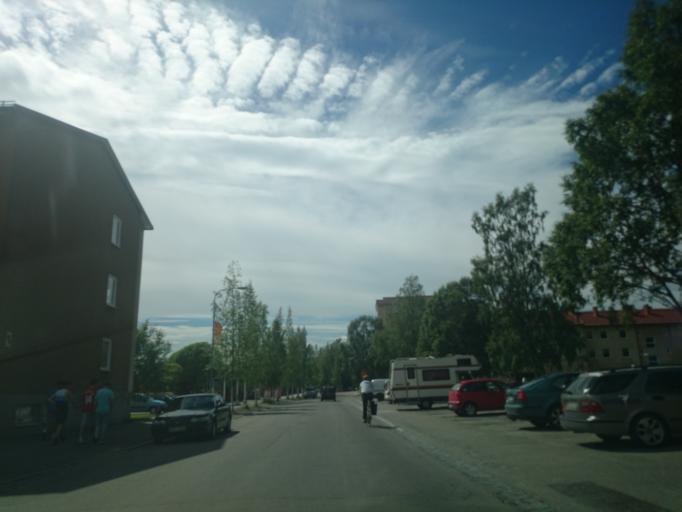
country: SE
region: Jaemtland
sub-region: OEstersunds Kommun
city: Ostersund
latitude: 63.1706
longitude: 14.6646
